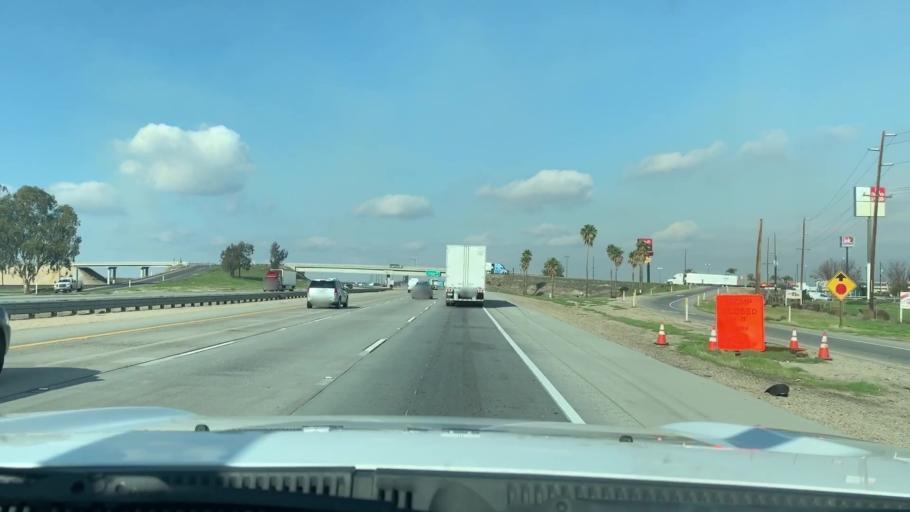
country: US
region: California
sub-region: Kern County
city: Shafter
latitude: 35.5273
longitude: -119.1886
